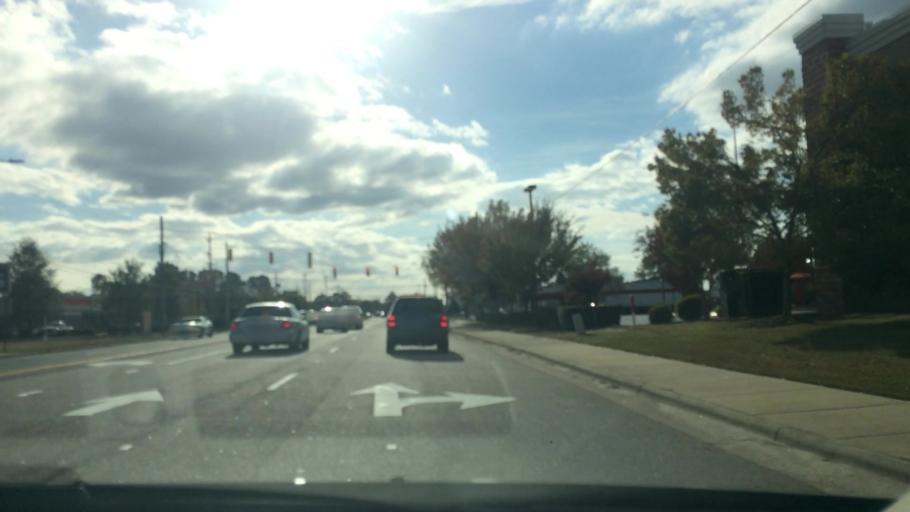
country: US
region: North Carolina
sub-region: Wayne County
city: Elroy
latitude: 35.3814
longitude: -77.9314
